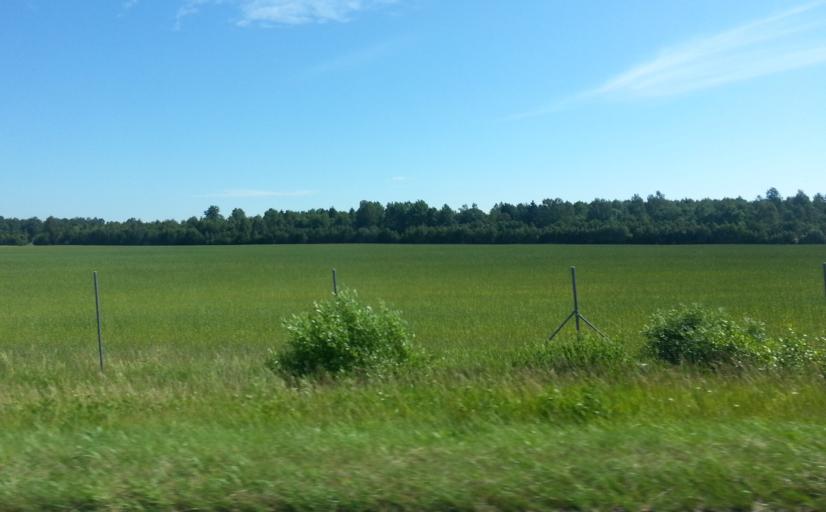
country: LT
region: Vilnius County
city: Ukmerge
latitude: 55.4824
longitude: 24.6388
